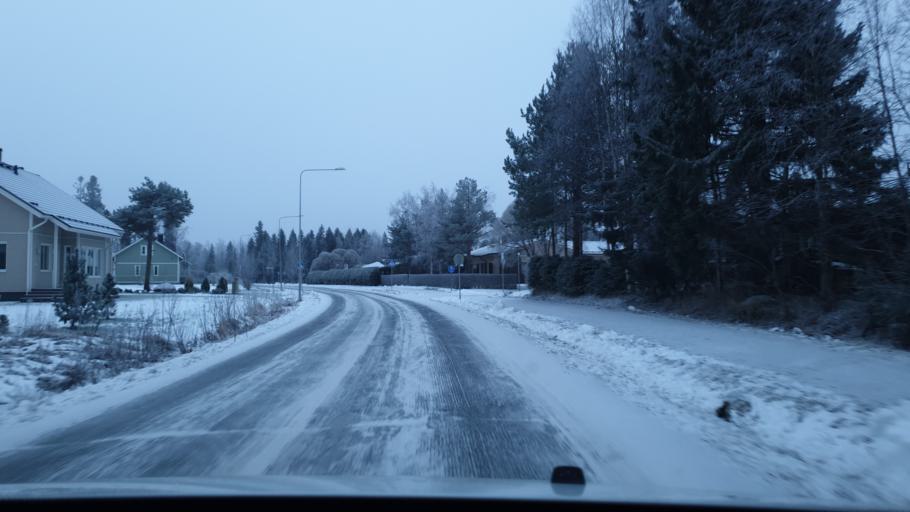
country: FI
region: Lapland
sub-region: Kemi-Tornio
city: Kemi
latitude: 65.7392
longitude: 24.6077
